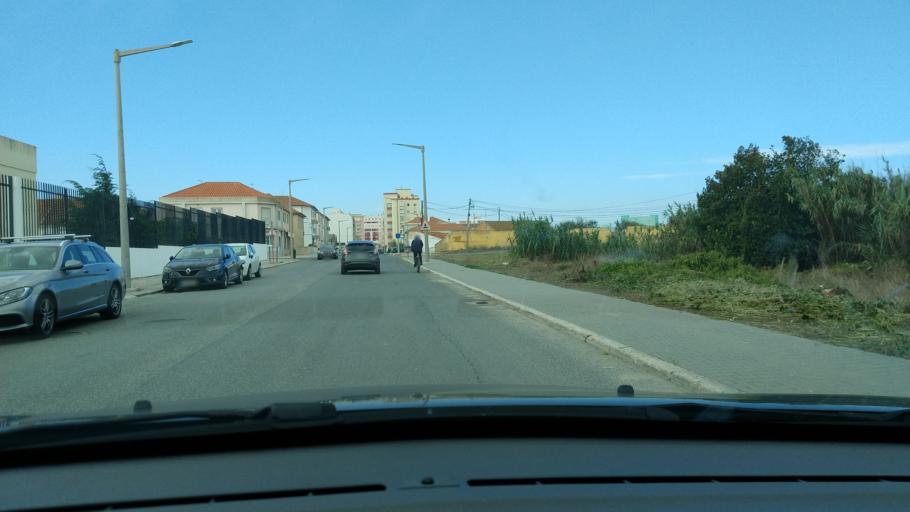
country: PT
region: Leiria
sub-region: Peniche
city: Peniche
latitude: 39.3609
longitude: -9.3845
